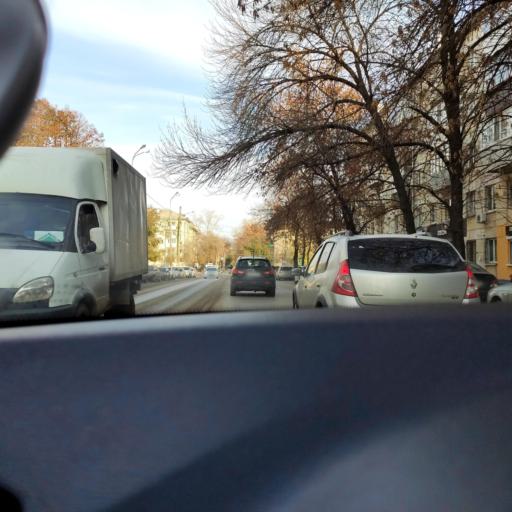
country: RU
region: Samara
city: Samara
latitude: 53.2087
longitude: 50.2302
